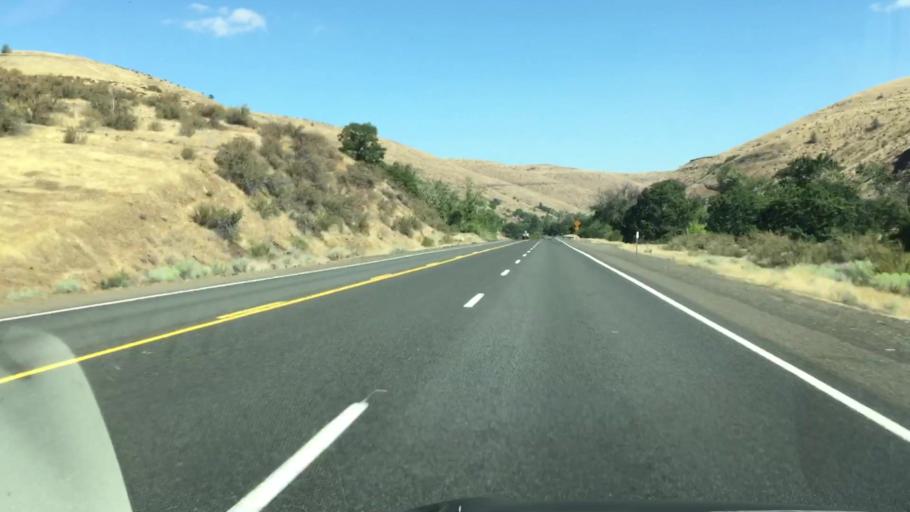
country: US
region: Oregon
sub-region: Wasco County
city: The Dalles
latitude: 45.2665
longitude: -121.1902
